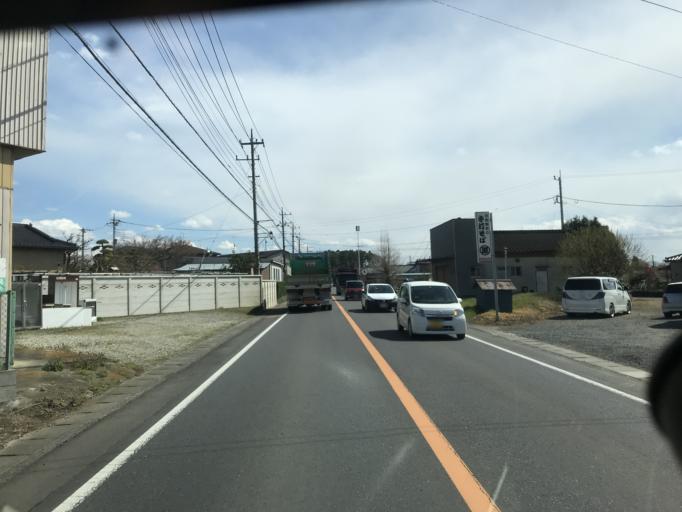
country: JP
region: Ibaraki
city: Yuki
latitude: 36.2389
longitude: 139.9318
